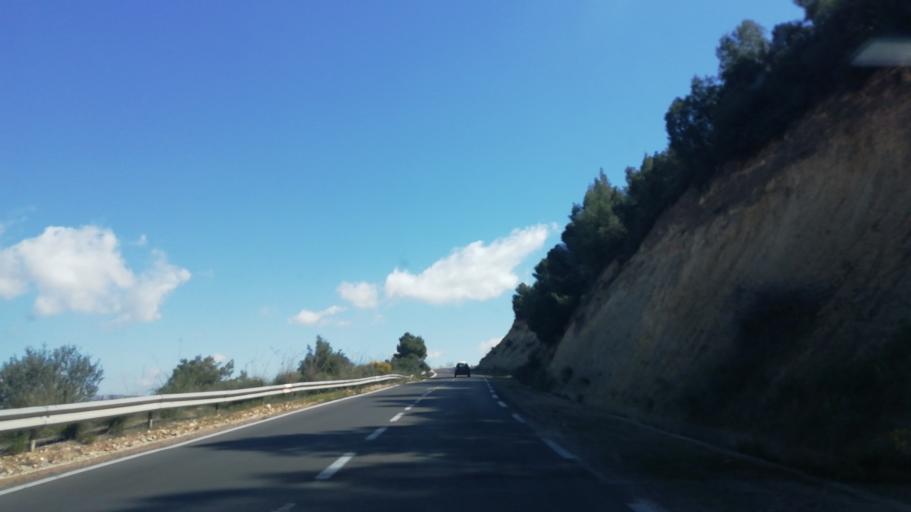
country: DZ
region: Mascara
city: Mascara
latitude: 35.4827
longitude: 0.1554
